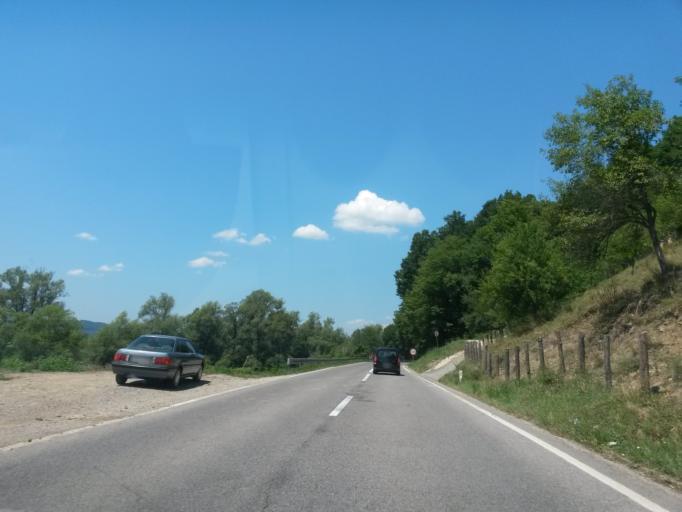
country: BA
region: Federation of Bosnia and Herzegovina
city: Lukavica
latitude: 44.9296
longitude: 18.1587
